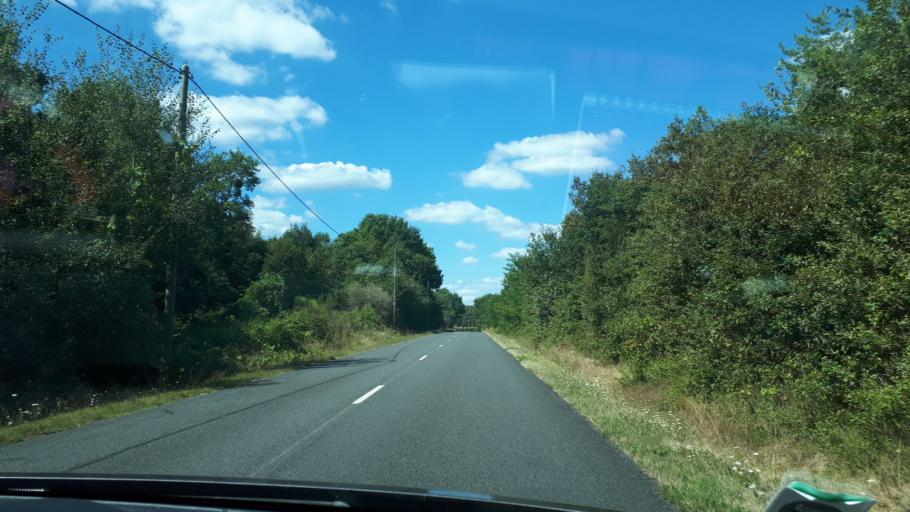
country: FR
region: Centre
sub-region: Departement du Loir-et-Cher
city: Neung-sur-Beuvron
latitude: 47.5344
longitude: 1.7568
